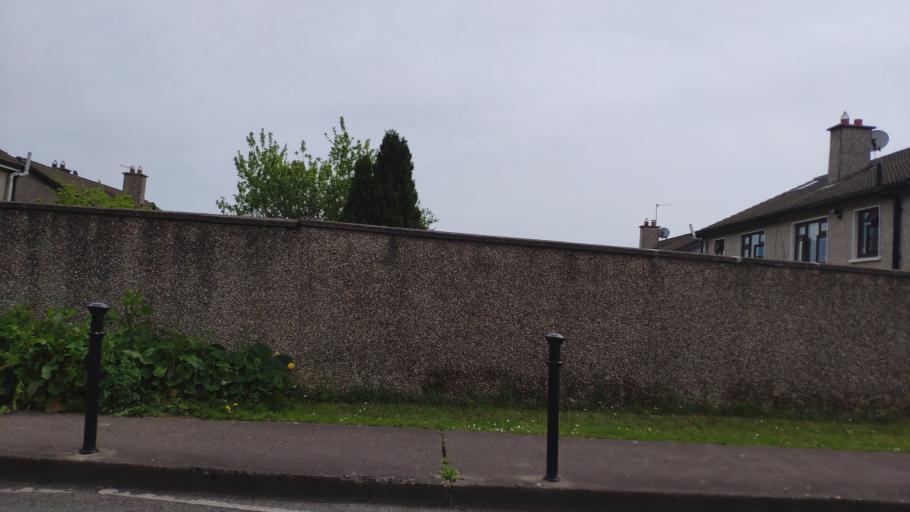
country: IE
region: Munster
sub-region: County Cork
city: Cork
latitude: 51.9213
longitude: -8.4591
